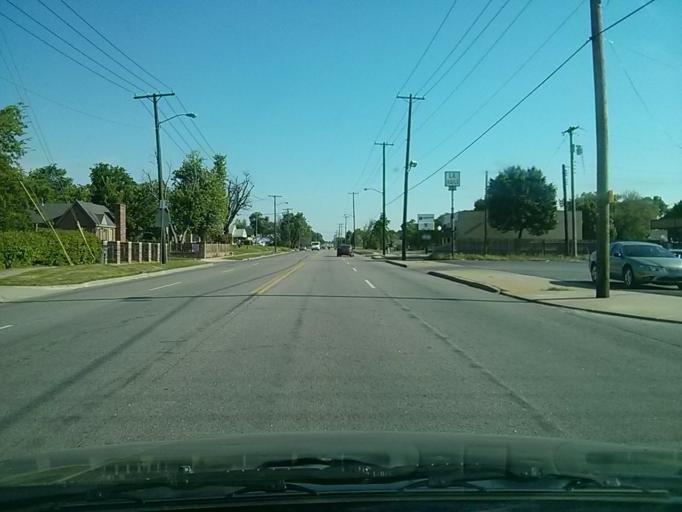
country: US
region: Oklahoma
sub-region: Tulsa County
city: Tulsa
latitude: 36.1841
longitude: -95.9935
